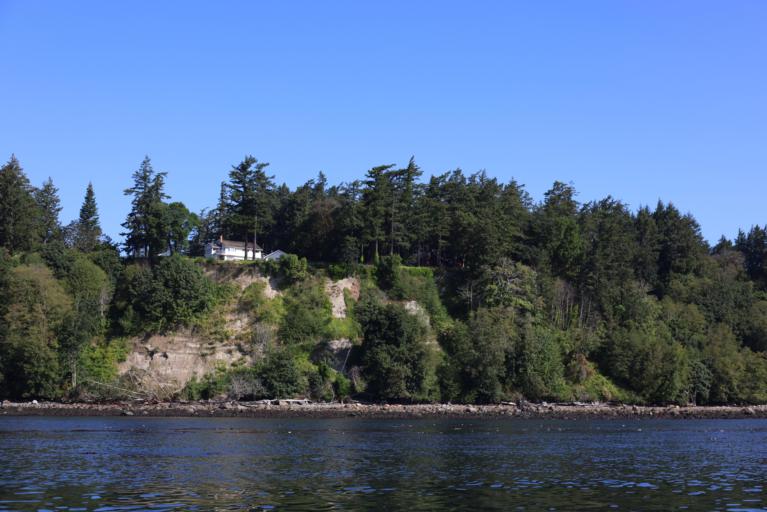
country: CA
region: British Columbia
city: Metchosin
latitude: 48.3705
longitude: -123.5241
